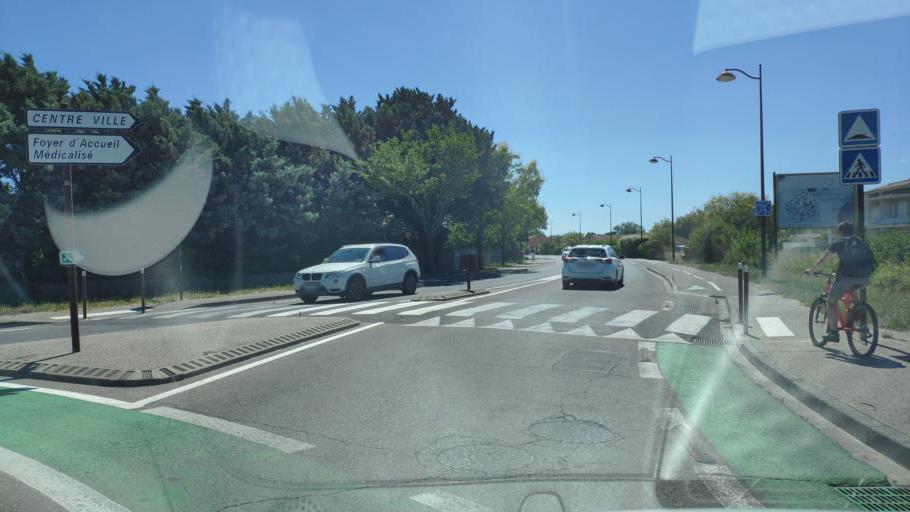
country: FR
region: Provence-Alpes-Cote d'Azur
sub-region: Departement du Vaucluse
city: L'Isle-sur-la-Sorgue
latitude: 43.9309
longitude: 5.0590
